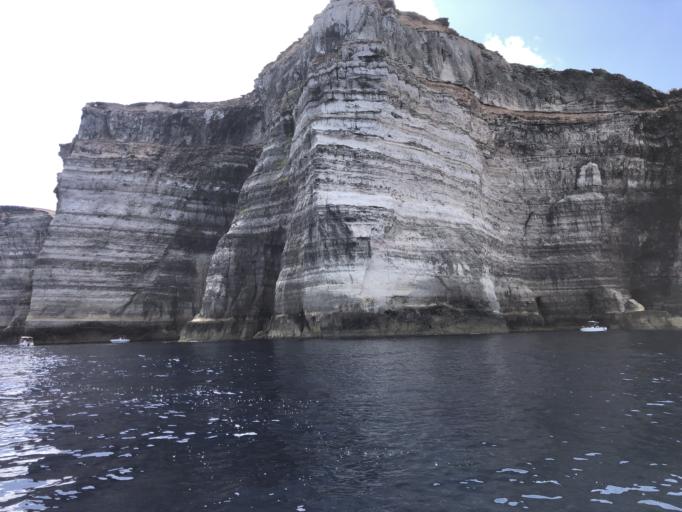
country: IT
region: Sicily
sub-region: Agrigento
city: Lampedusa
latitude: 35.5291
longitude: 12.5258
